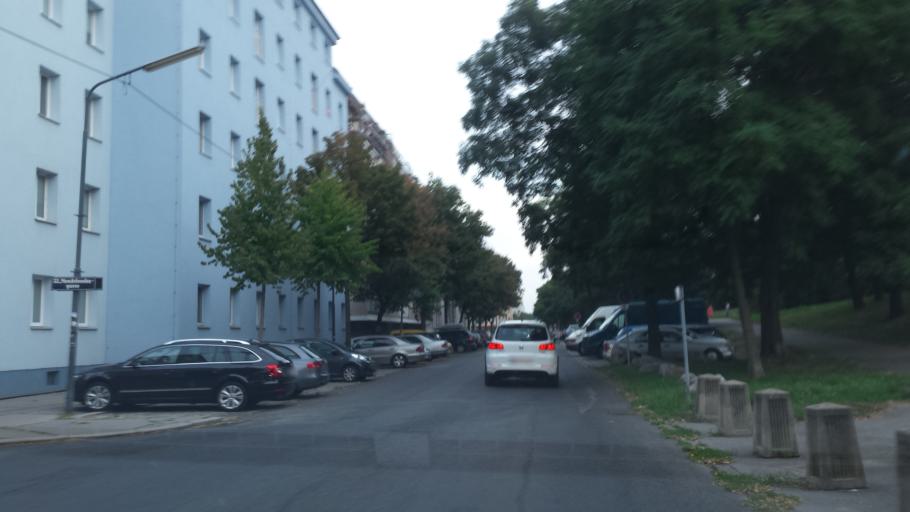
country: AT
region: Vienna
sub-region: Wien Stadt
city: Vienna
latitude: 48.2242
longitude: 16.4224
